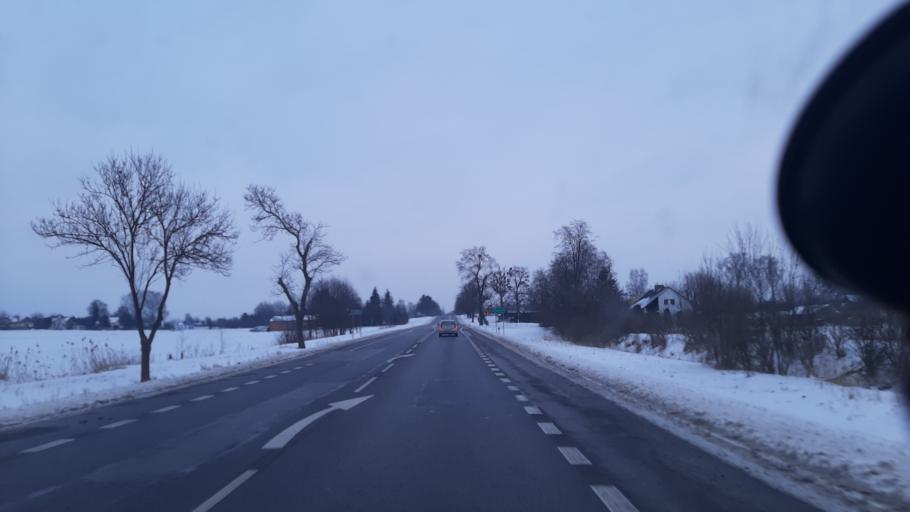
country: PL
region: Lublin Voivodeship
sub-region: Powiat lubelski
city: Garbow
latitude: 51.3607
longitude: 22.3102
